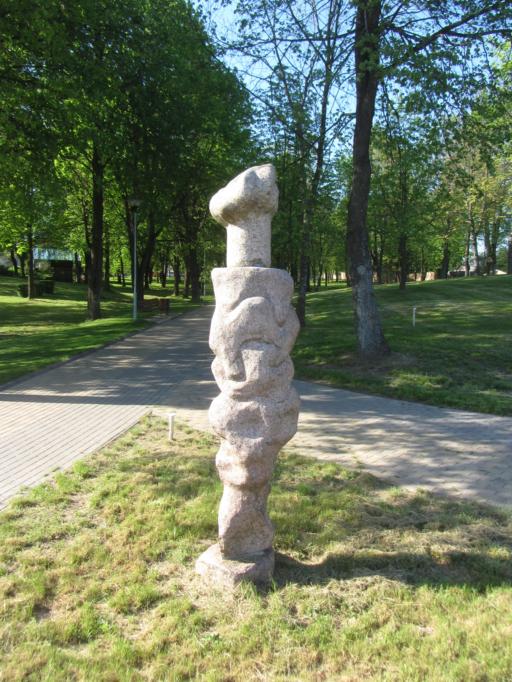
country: LT
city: Moletai
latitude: 55.2313
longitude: 25.4262
